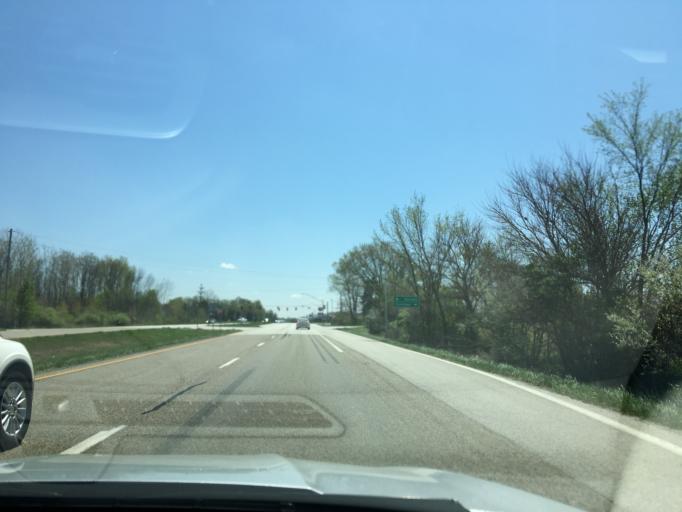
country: US
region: Indiana
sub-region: Boone County
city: Thorntown
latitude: 40.1284
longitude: -86.5635
